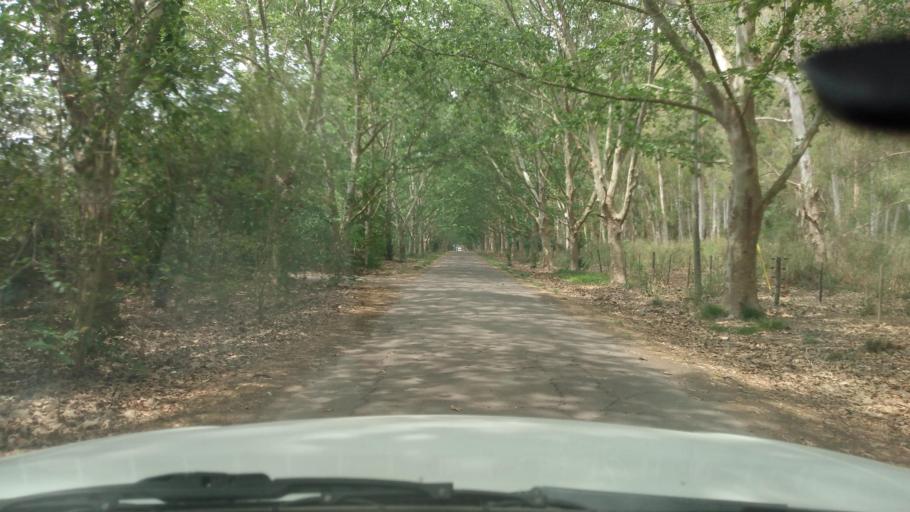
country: AR
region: Buenos Aires
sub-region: Partido de Lujan
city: Lujan
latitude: -34.5564
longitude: -59.1902
